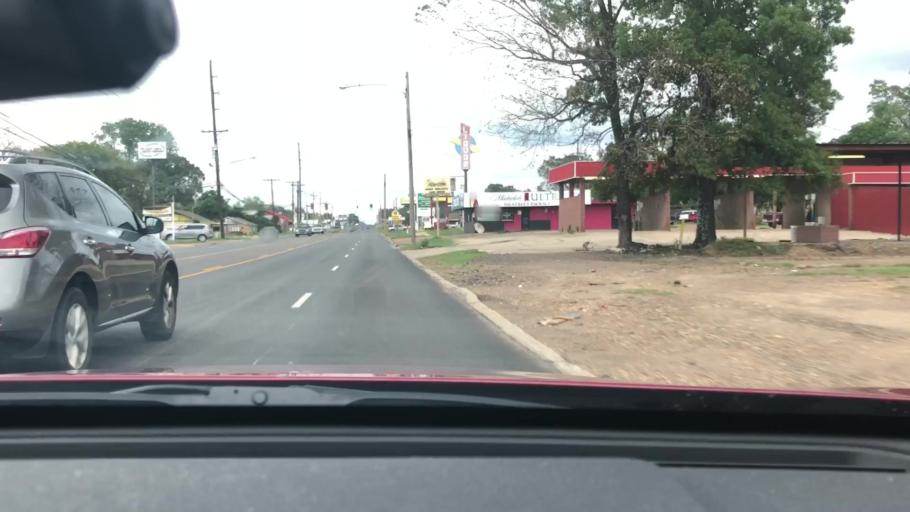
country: US
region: Arkansas
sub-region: Miller County
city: Texarkana
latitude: 33.4307
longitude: -94.0249
